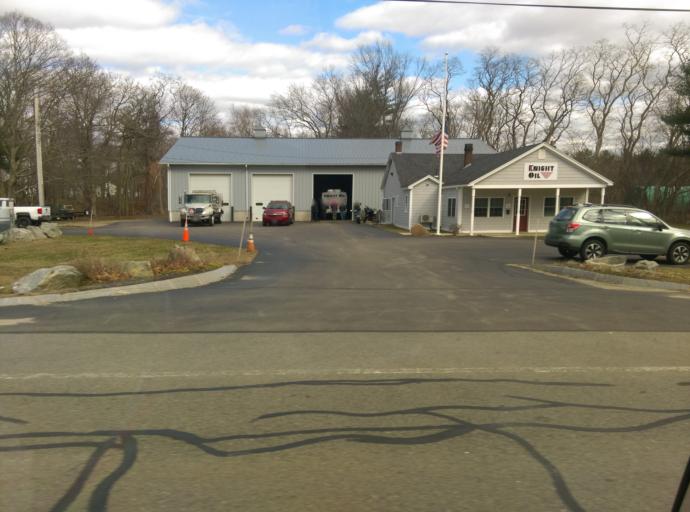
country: US
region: New Hampshire
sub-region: Rockingham County
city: Seabrook
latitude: 42.8670
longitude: -70.8869
